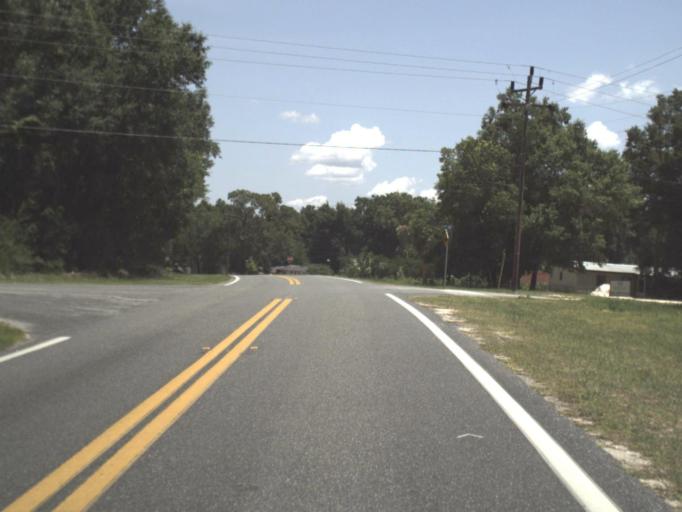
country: US
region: Florida
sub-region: Taylor County
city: Steinhatchee
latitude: 29.6688
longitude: -83.3703
